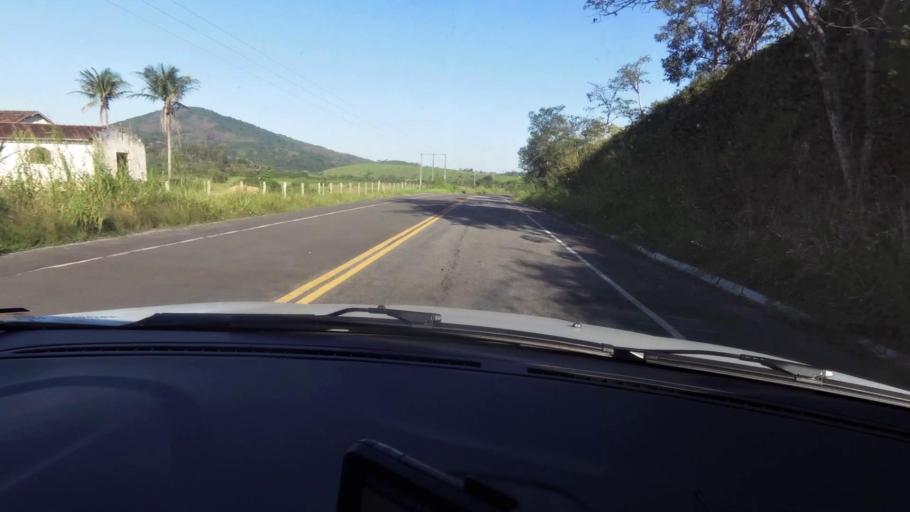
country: BR
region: Espirito Santo
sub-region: Piuma
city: Piuma
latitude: -20.7325
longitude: -40.6517
